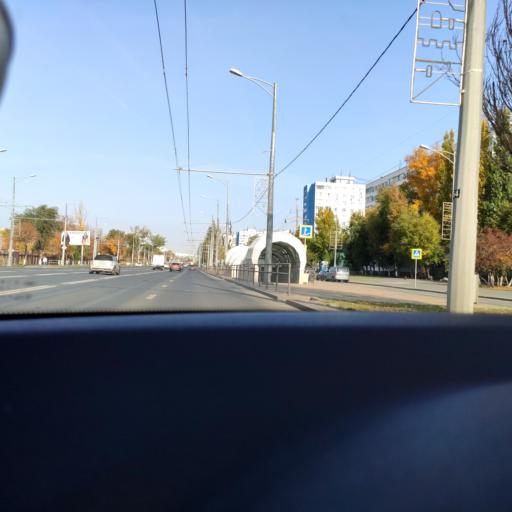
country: RU
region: Samara
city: Samara
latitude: 53.2363
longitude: 50.2017
